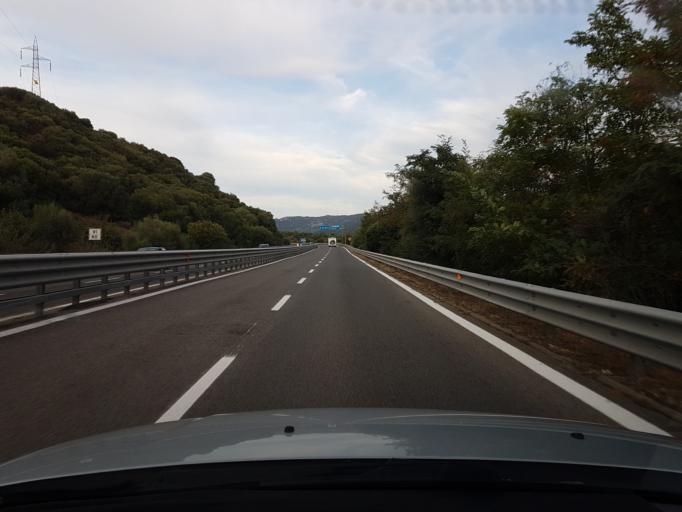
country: IT
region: Sardinia
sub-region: Provincia di Nuoro
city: Orune
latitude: 40.3686
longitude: 9.3803
